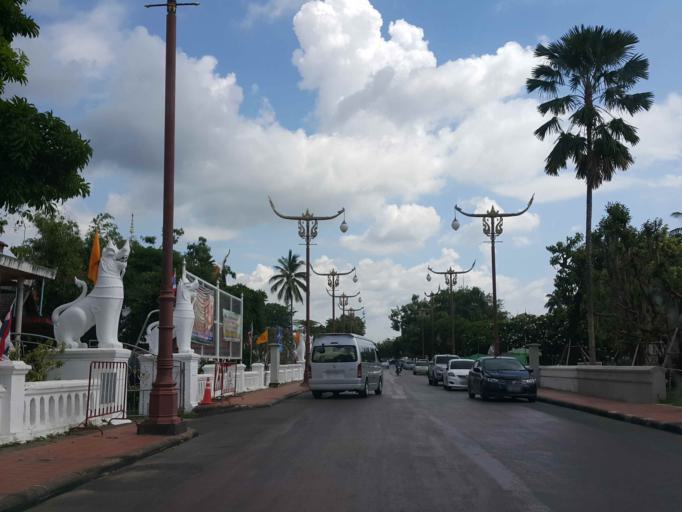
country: TH
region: Nan
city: Nan
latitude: 18.7738
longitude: 100.7720
